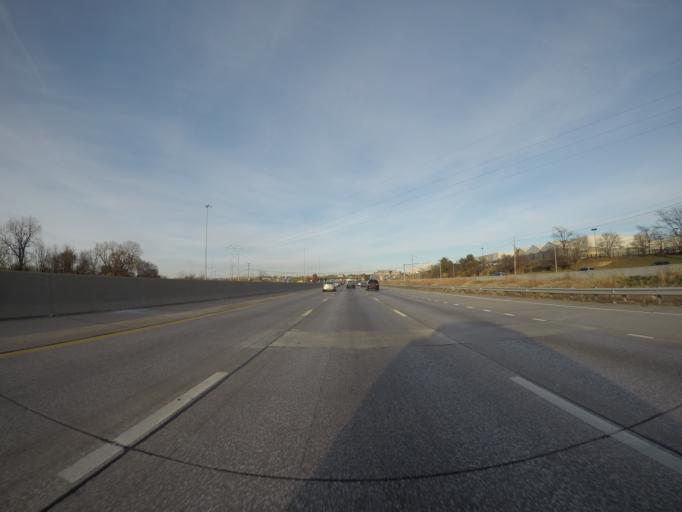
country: US
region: Kansas
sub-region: Johnson County
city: Overland Park
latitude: 38.9896
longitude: -94.7011
